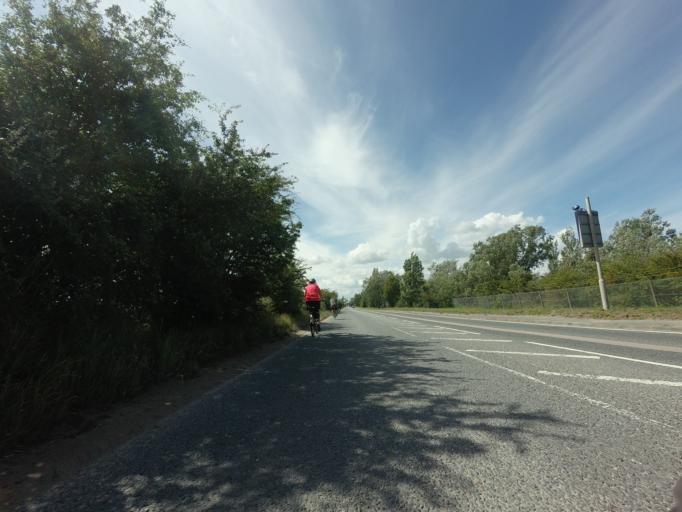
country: GB
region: England
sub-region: Medway
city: Allhallows
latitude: 51.4440
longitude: 0.6846
